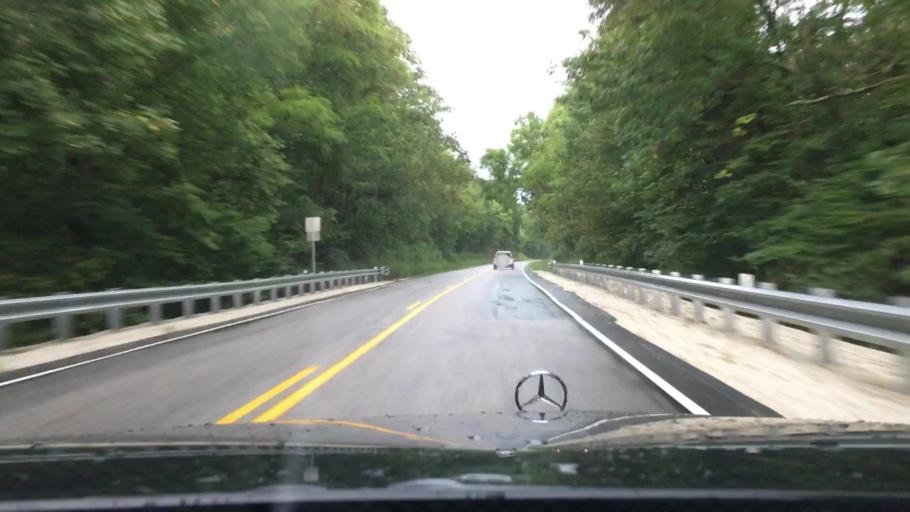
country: US
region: Virginia
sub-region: Amherst County
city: Amherst
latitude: 37.6903
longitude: -79.0265
